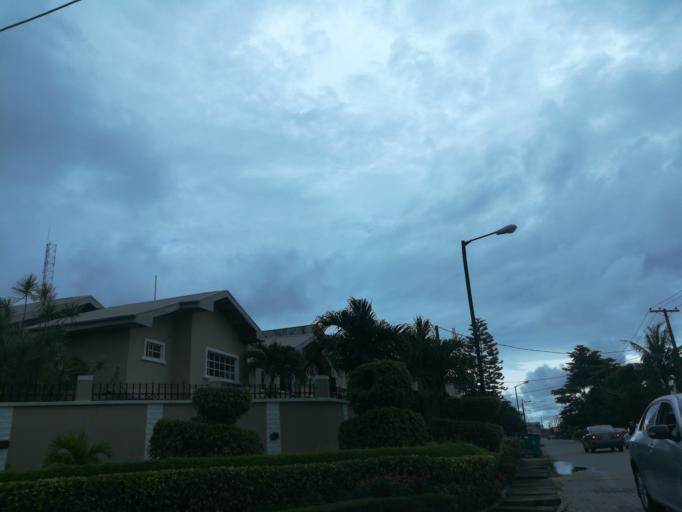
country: NG
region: Lagos
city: Ikoyi
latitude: 6.4417
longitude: 3.4685
